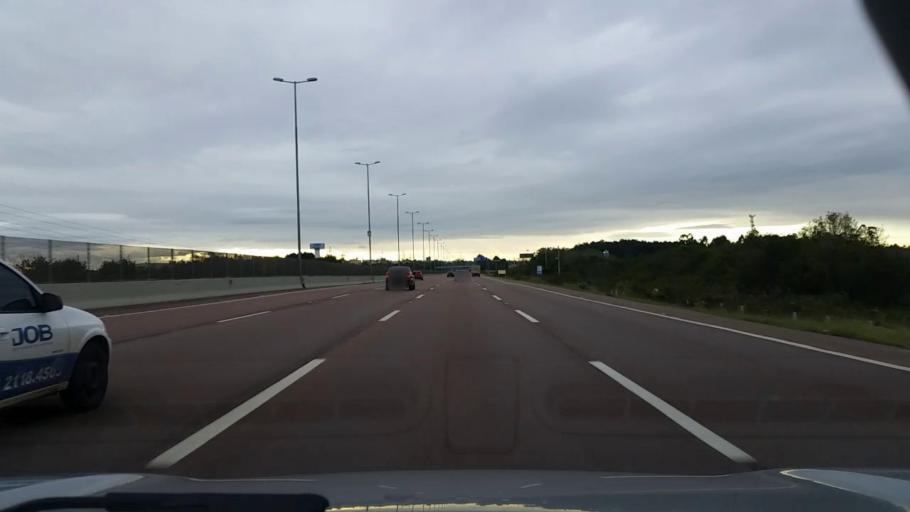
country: BR
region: Rio Grande do Sul
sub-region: Cachoeirinha
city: Cachoeirinha
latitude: -29.9547
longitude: -51.0685
